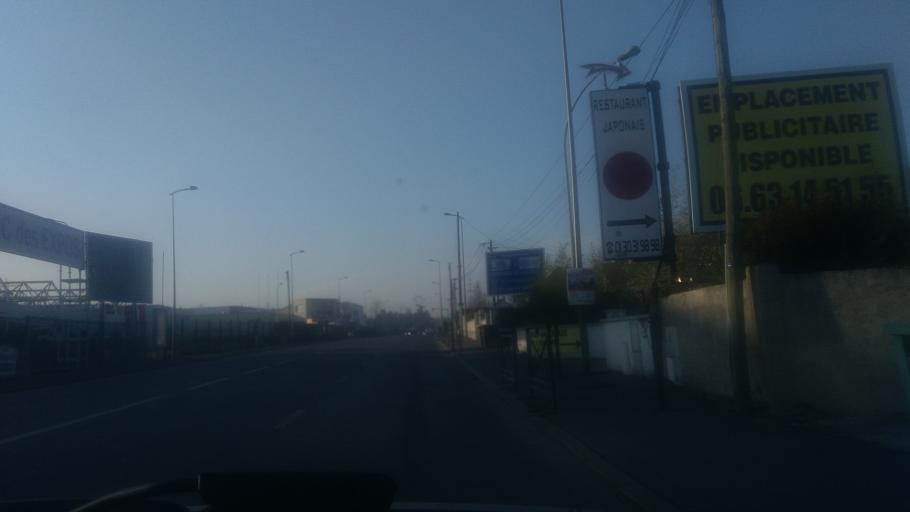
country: FR
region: Ile-de-France
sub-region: Departement du Val-d'Oise
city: Cergy-Pontoise
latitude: 49.0463
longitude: 2.0843
